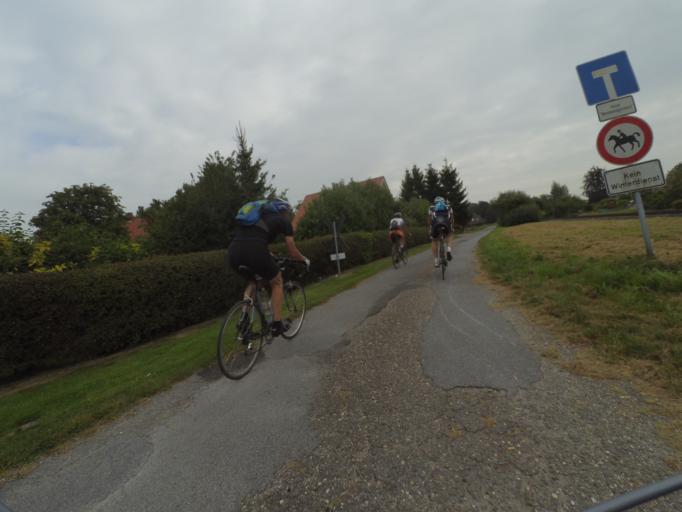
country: DE
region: Lower Saxony
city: Bad Bentheim
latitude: 52.2960
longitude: 7.1091
